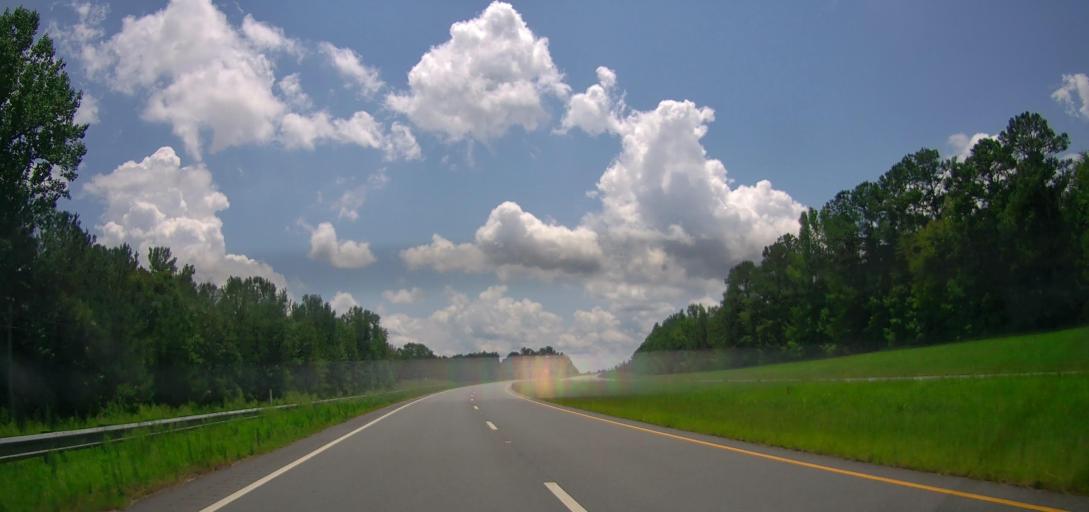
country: US
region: Georgia
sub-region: Upson County
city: Thomaston
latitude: 32.7637
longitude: -84.2443
